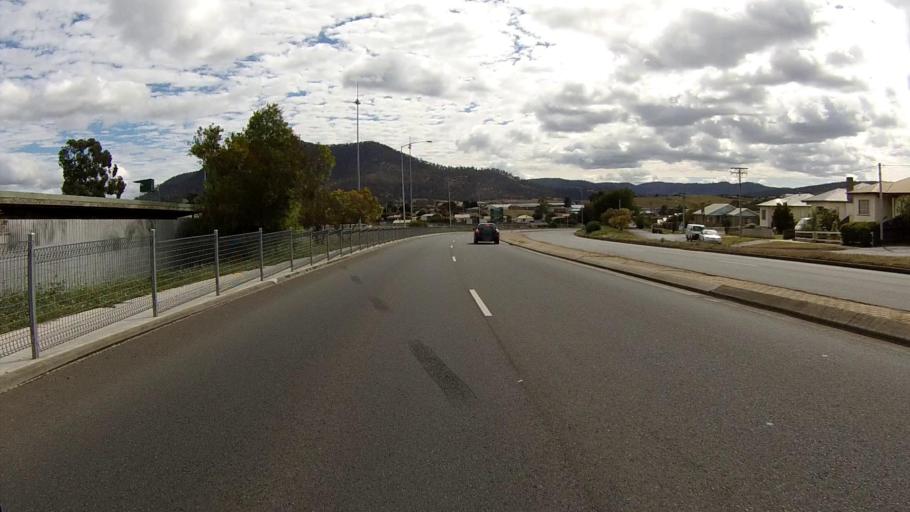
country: AU
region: Tasmania
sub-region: Glenorchy
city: Goodwood
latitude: -42.8250
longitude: 147.2905
